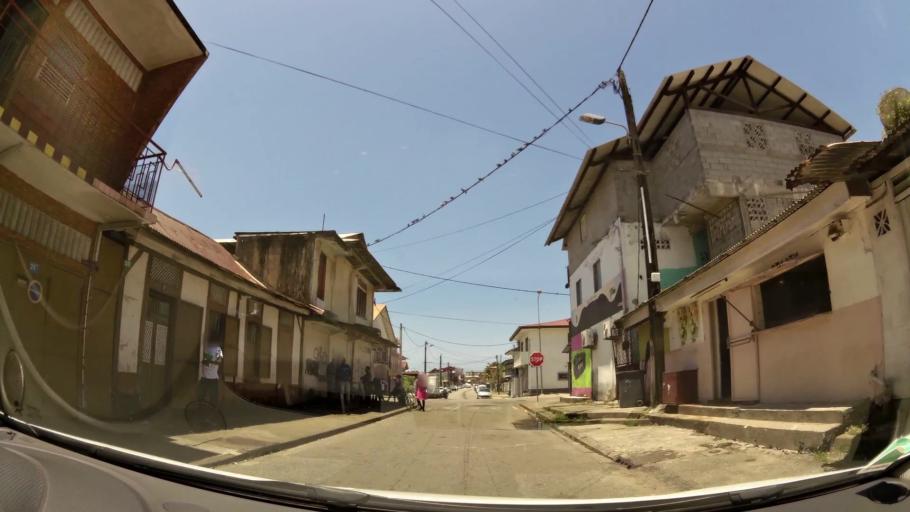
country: GF
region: Guyane
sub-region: Guyane
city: Cayenne
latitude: 4.9339
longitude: -52.3334
